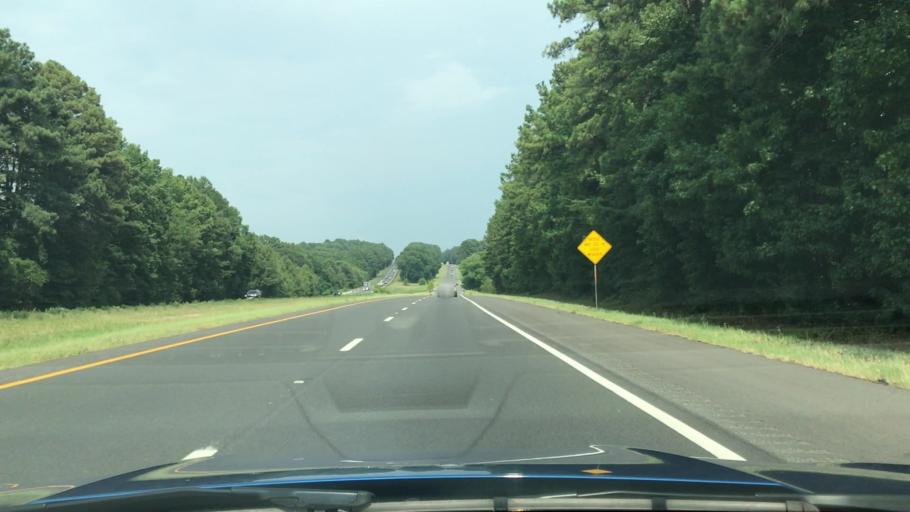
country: US
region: Texas
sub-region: Harrison County
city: Hallsville
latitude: 32.4685
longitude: -94.6085
